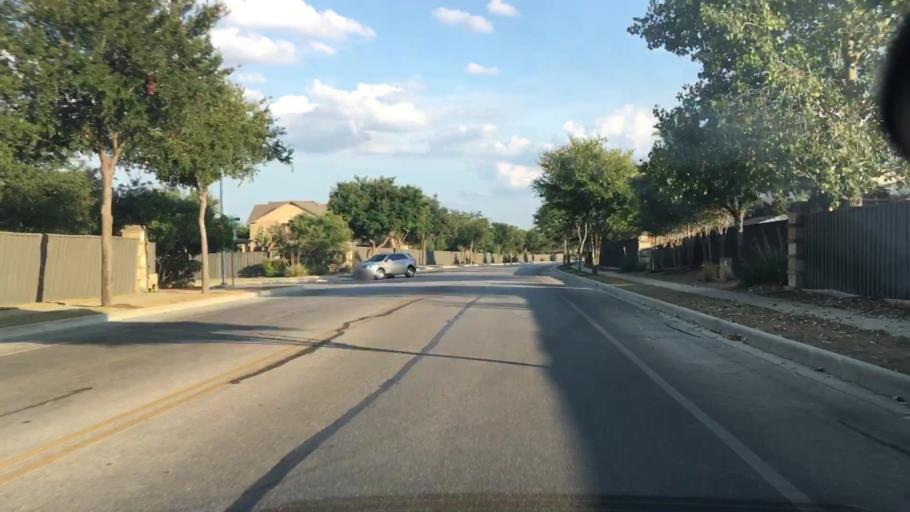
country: US
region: Texas
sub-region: Guadalupe County
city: Cibolo
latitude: 29.5830
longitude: -98.2415
